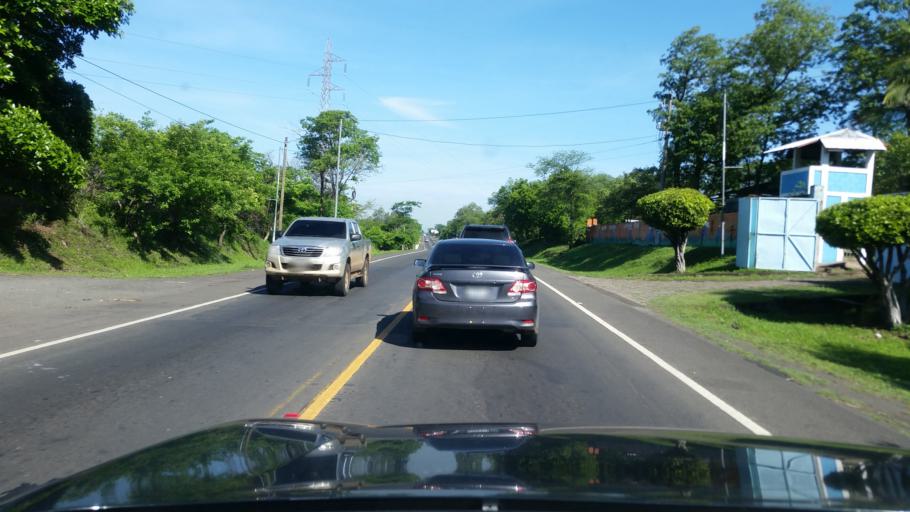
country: NI
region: Chinandega
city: Chichigalpa
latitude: 12.6030
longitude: -87.0488
